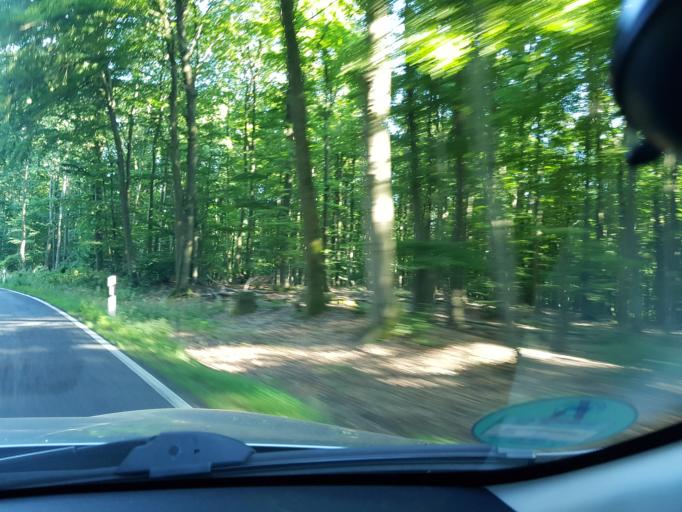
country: DE
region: Rheinland-Pfalz
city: Arzbach
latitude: 50.4008
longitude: 7.7797
